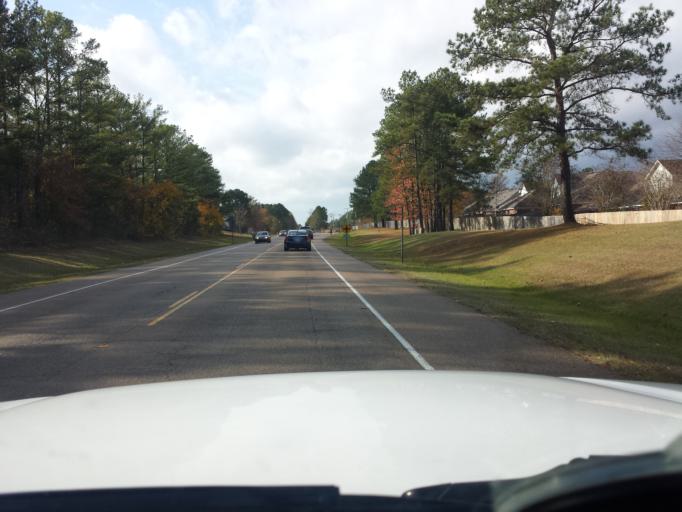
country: US
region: Mississippi
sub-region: Madison County
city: Ridgeland
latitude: 32.3917
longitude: -90.0312
